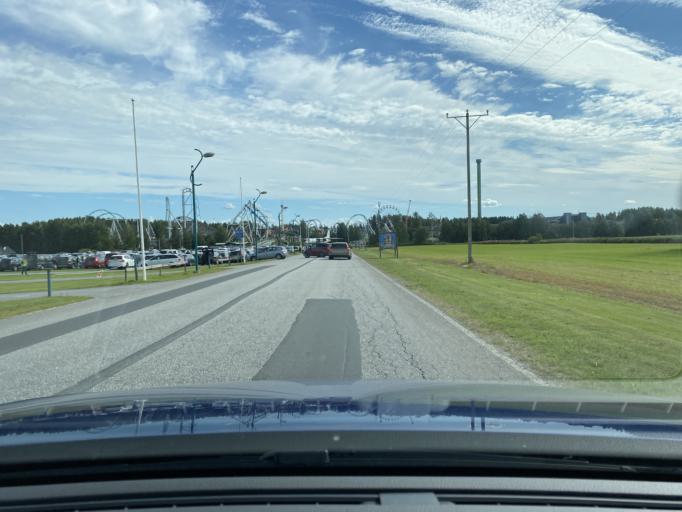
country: FI
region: Southern Ostrobothnia
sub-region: Seinaejoki
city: Alahaermae
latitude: 63.2293
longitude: 22.8474
